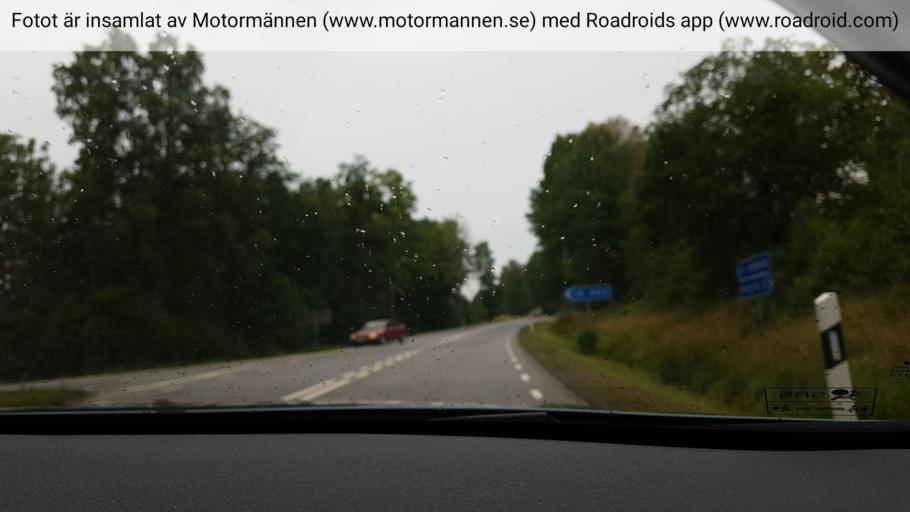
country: SE
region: Joenkoeping
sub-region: Varnamo Kommun
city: Bor
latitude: 57.2292
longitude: 14.1547
